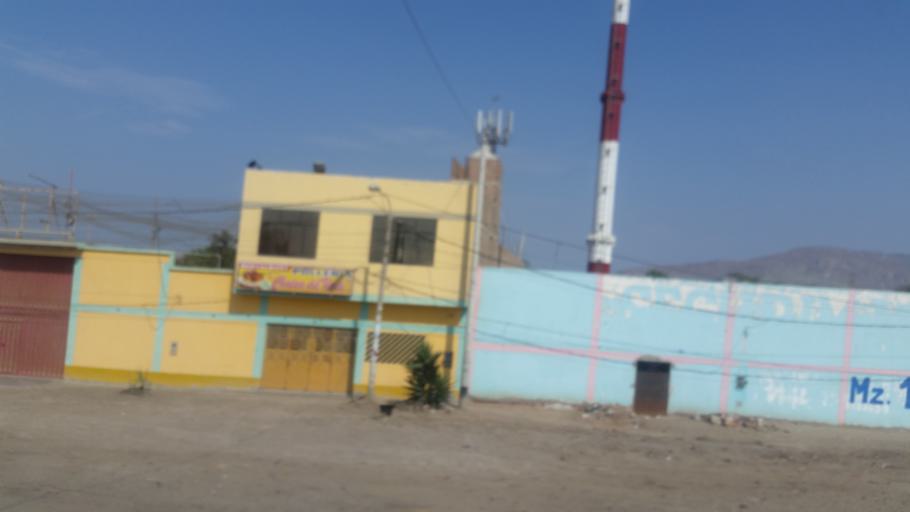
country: PE
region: Lambayeque
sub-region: Provincia de Chiclayo
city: Reque
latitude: -6.8324
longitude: -79.8293
